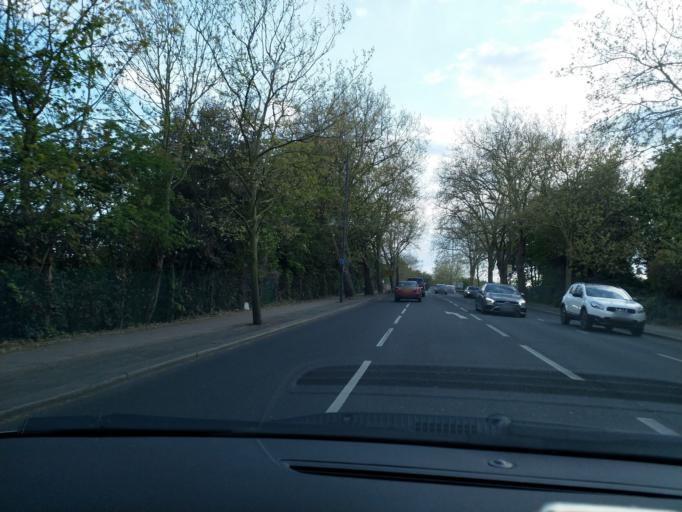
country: GB
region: England
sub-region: Greater London
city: Acton
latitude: 51.4786
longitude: -0.2618
